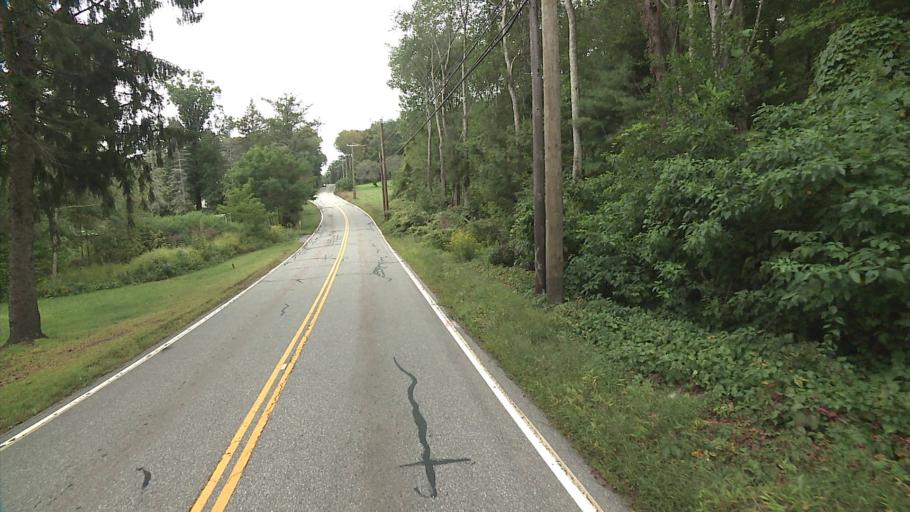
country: US
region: Connecticut
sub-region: Tolland County
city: Storrs
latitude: 41.8625
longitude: -72.2684
